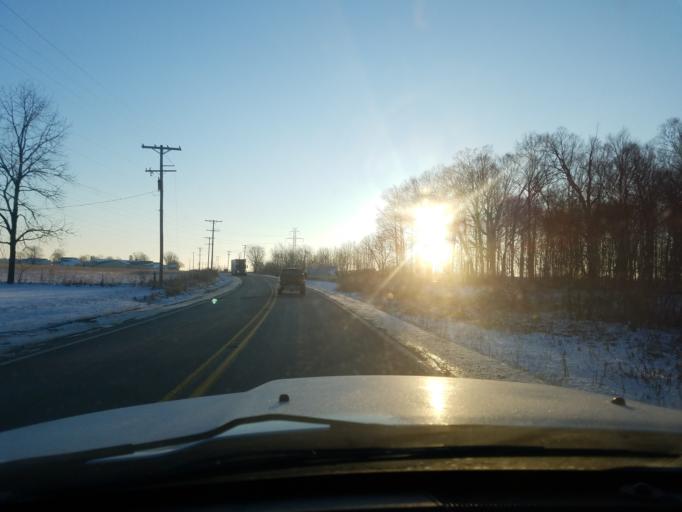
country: US
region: Indiana
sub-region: Marshall County
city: Bremen
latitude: 41.4475
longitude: -86.0854
